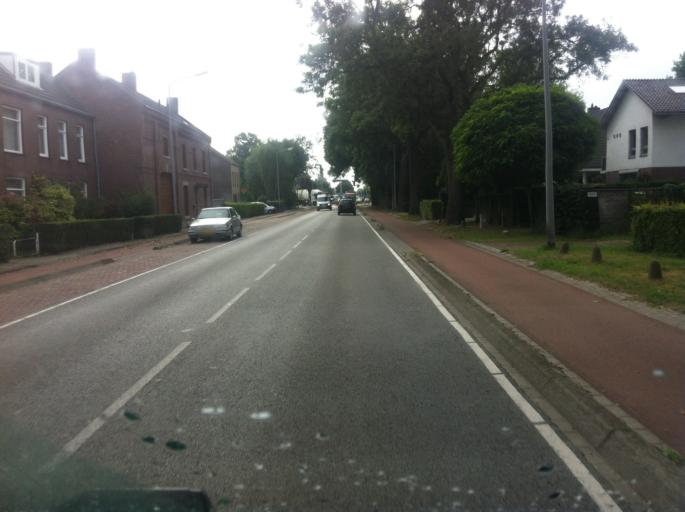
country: NL
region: Limburg
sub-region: Gemeente Maastricht
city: Maastricht
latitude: 50.8645
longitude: 5.6721
